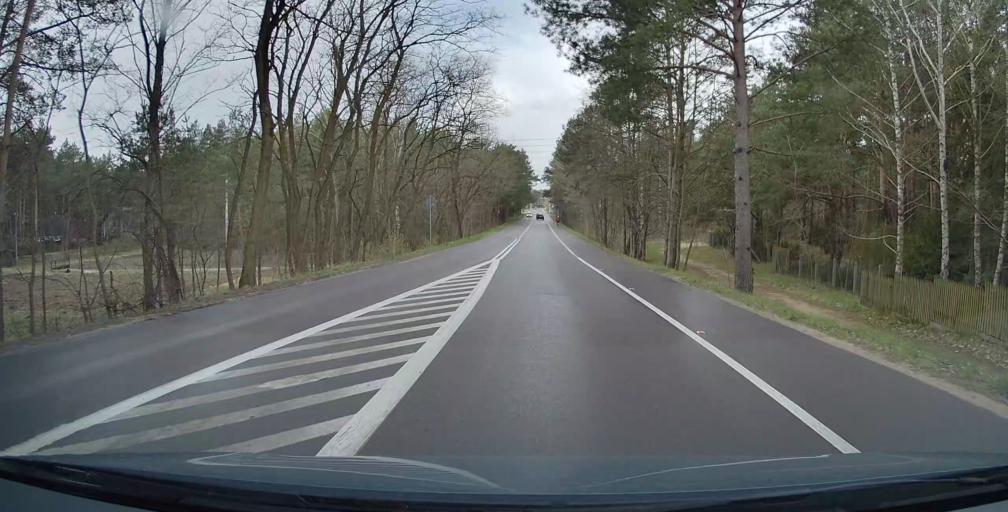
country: PL
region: Masovian Voivodeship
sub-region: Powiat wyszkowski
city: Dlugosiodlo
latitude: 52.7695
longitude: 21.5581
